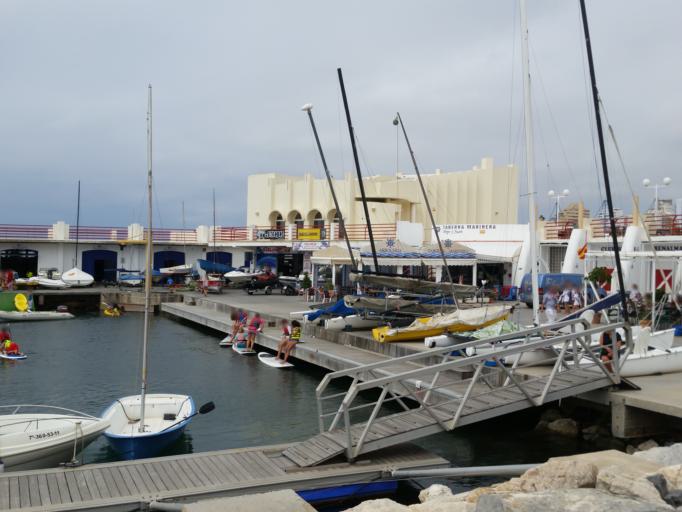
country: ES
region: Andalusia
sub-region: Provincia de Malaga
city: Torremolinos
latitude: 36.5950
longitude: -4.5142
